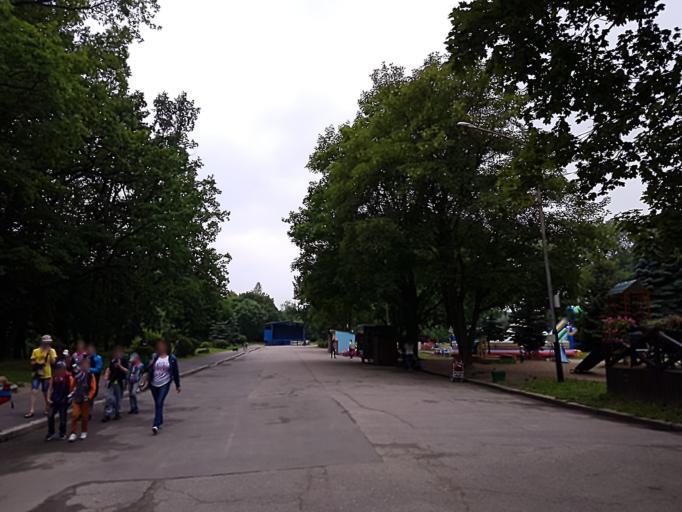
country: RU
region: Kaliningrad
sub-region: Gorod Kaliningrad
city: Kaliningrad
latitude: 54.6930
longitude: 20.5149
